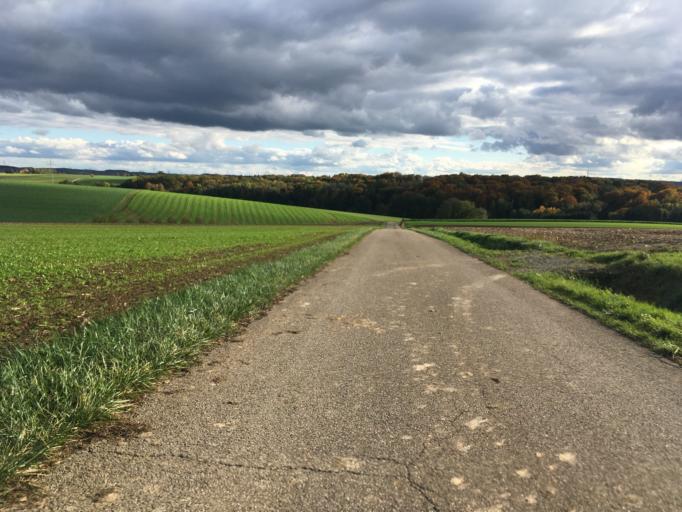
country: DE
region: Baden-Wuerttemberg
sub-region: Regierungsbezirk Stuttgart
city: Kuenzelsau
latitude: 49.2568
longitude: 9.6627
